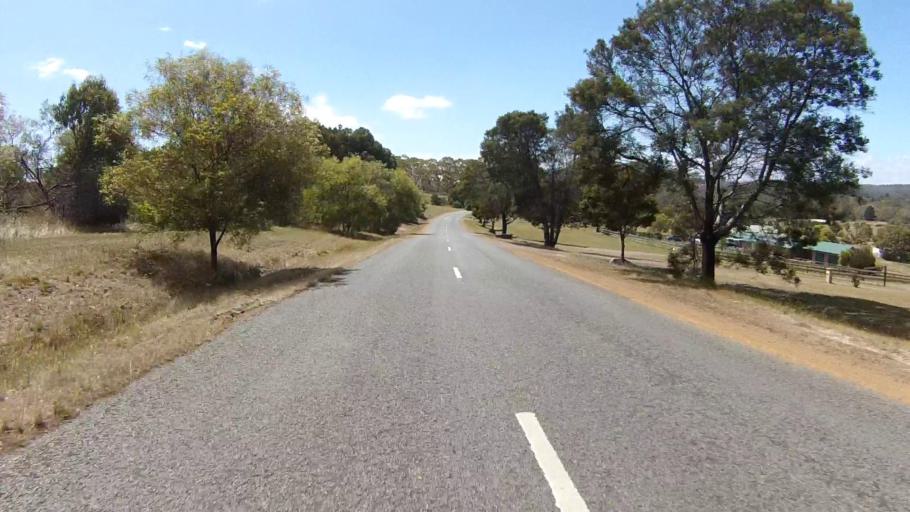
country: AU
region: Tasmania
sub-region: Clarence
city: Sandford
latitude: -42.9953
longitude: 147.4769
